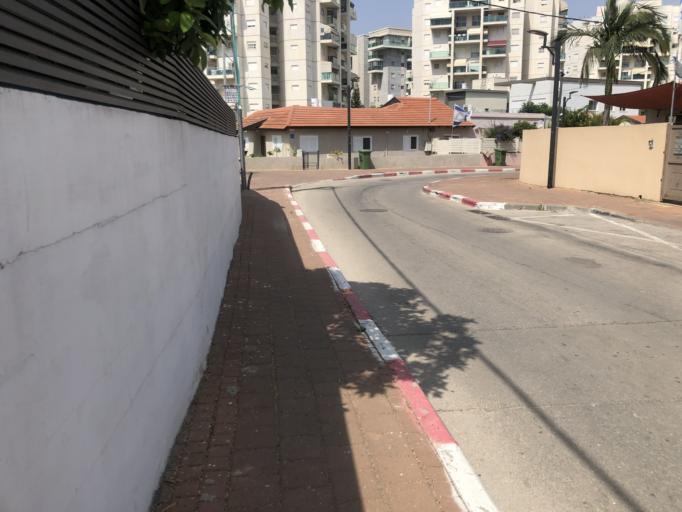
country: IL
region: Central District
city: Rosh Ha'Ayin
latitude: 32.0957
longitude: 34.9398
